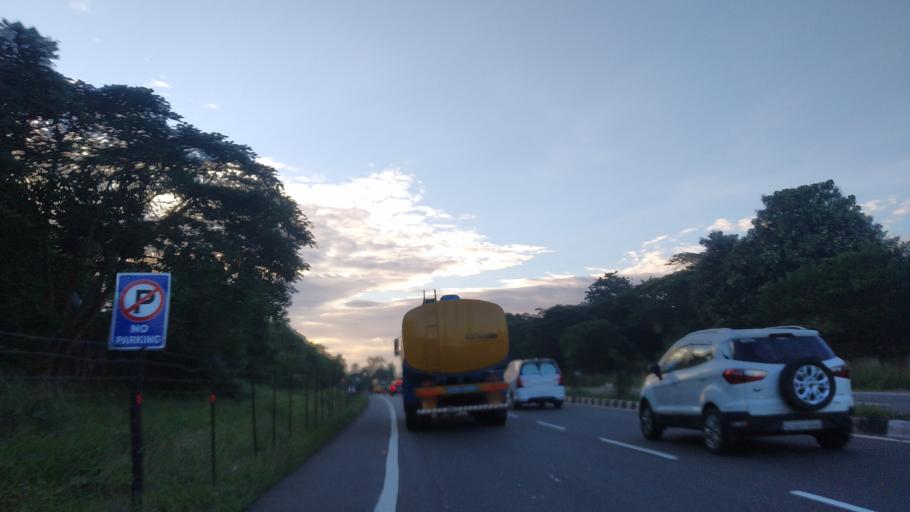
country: IN
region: Kerala
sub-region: Ernakulam
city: Elur
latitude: 10.0687
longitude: 76.3079
